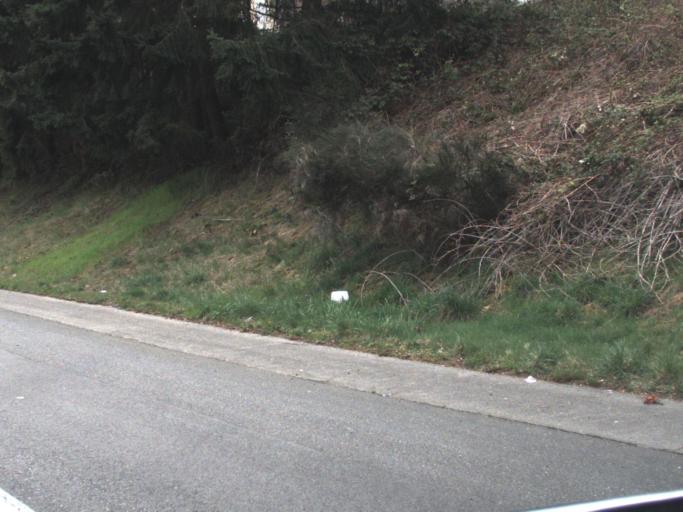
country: US
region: Washington
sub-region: King County
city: Kent
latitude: 47.3885
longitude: -122.2784
